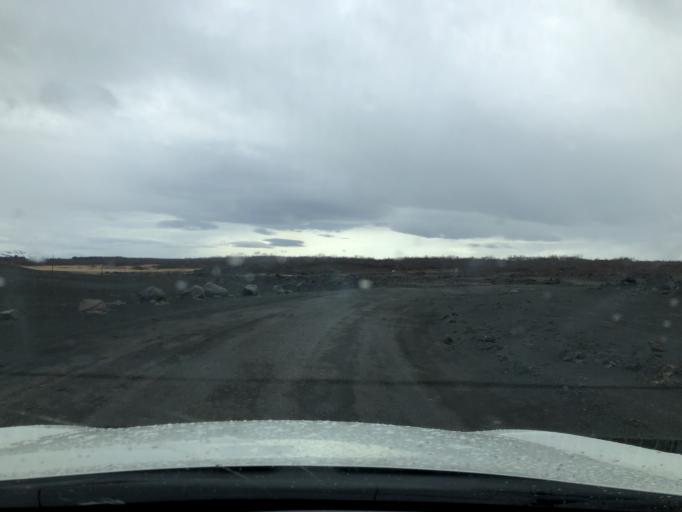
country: IS
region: Northeast
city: Laugar
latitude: 65.6076
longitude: -16.8885
